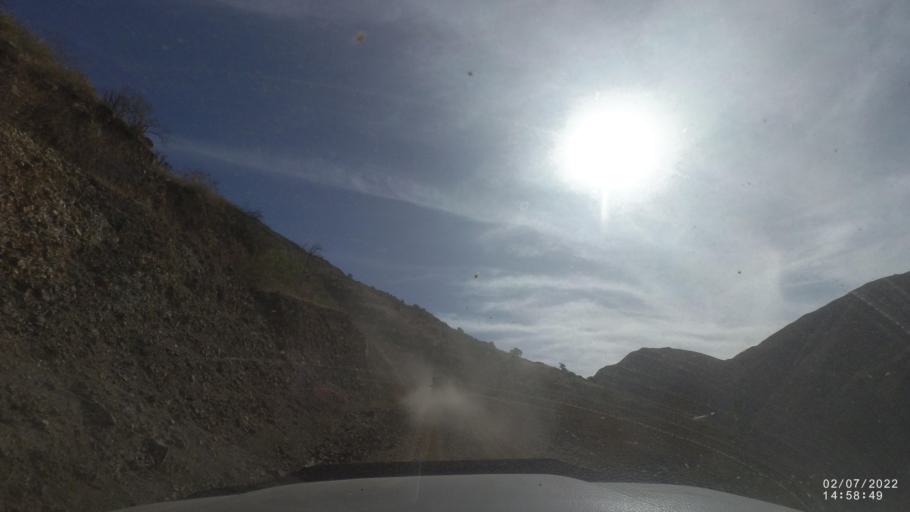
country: BO
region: Cochabamba
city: Irpa Irpa
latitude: -17.8550
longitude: -66.4377
